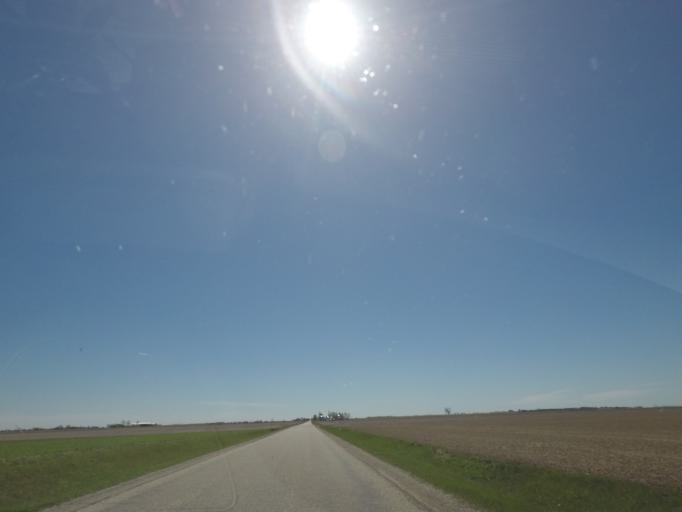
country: US
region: Illinois
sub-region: Logan County
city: Atlanta
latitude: 40.2090
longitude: -89.1944
